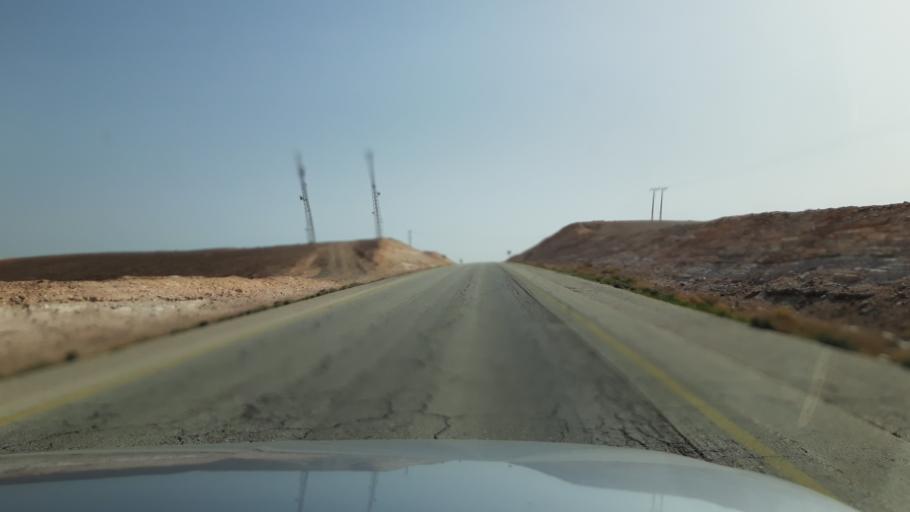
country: JO
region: Amman
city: Al Azraq ash Shamali
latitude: 31.8515
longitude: 36.6756
